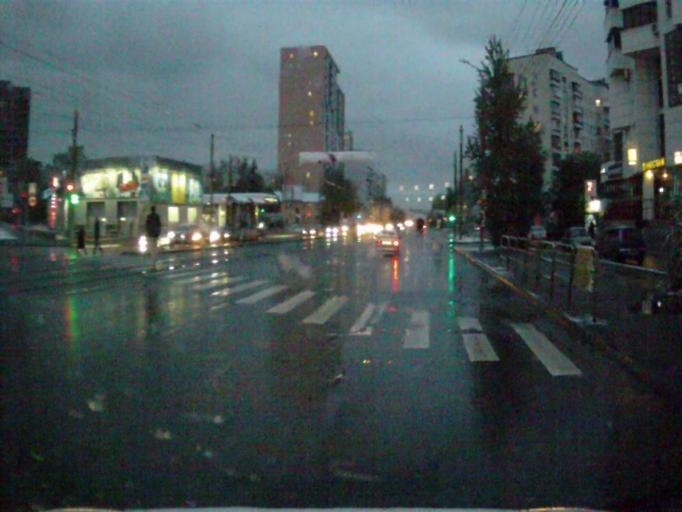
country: RU
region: Chelyabinsk
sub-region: Gorod Chelyabinsk
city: Chelyabinsk
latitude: 55.1501
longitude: 61.3903
